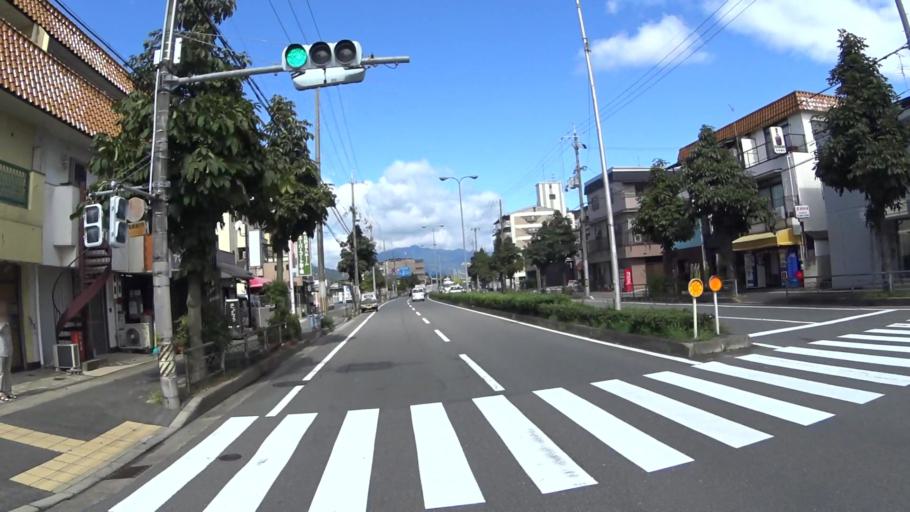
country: JP
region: Kyoto
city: Muko
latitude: 34.9793
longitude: 135.7106
